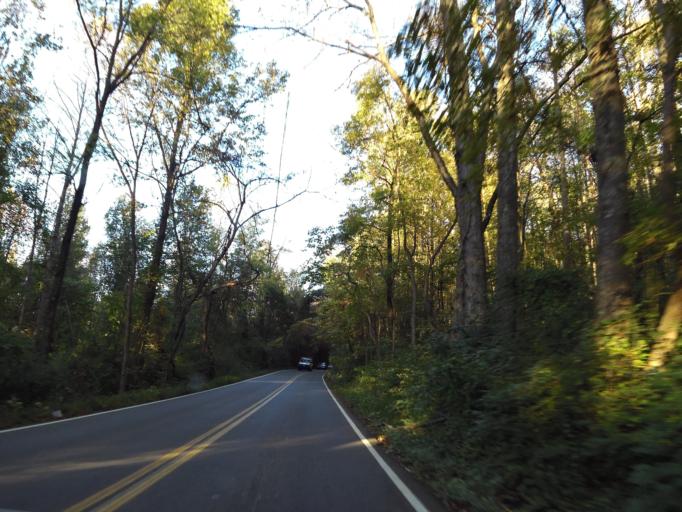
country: US
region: Tennessee
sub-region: Knox County
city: Knoxville
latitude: 36.0421
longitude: -83.9544
